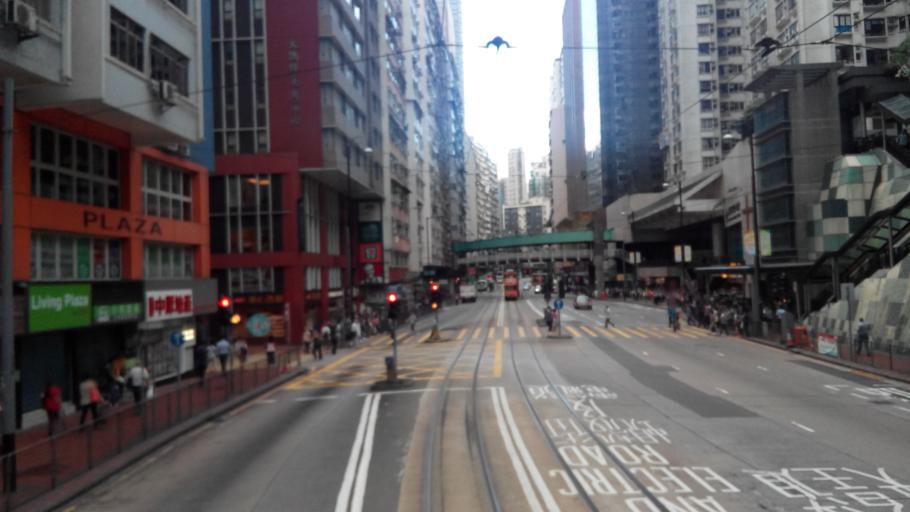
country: HK
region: Wanchai
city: Wan Chai
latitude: 22.2878
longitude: 114.1932
